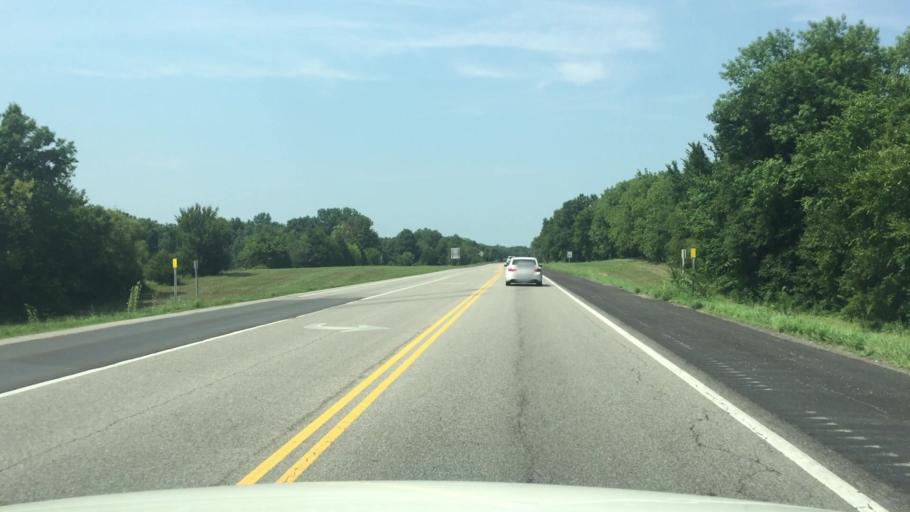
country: US
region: Kansas
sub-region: Crawford County
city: Pittsburg
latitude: 37.3976
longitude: -94.7196
